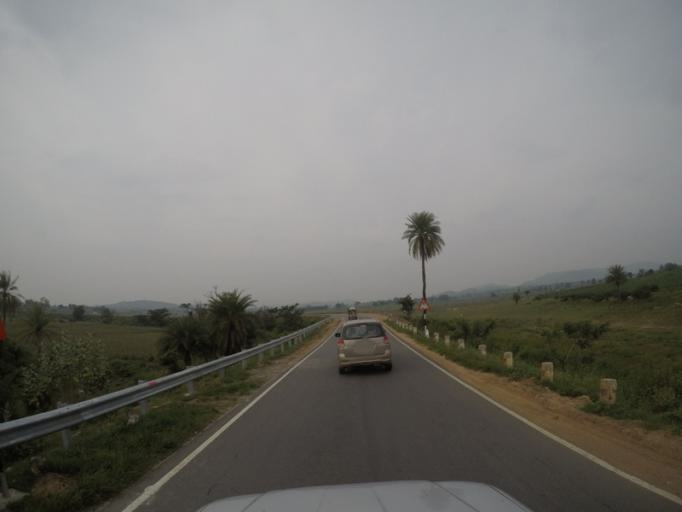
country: IN
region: Karnataka
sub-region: Chikmagalur
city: Chikmagalur
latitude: 13.2646
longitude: 75.8464
